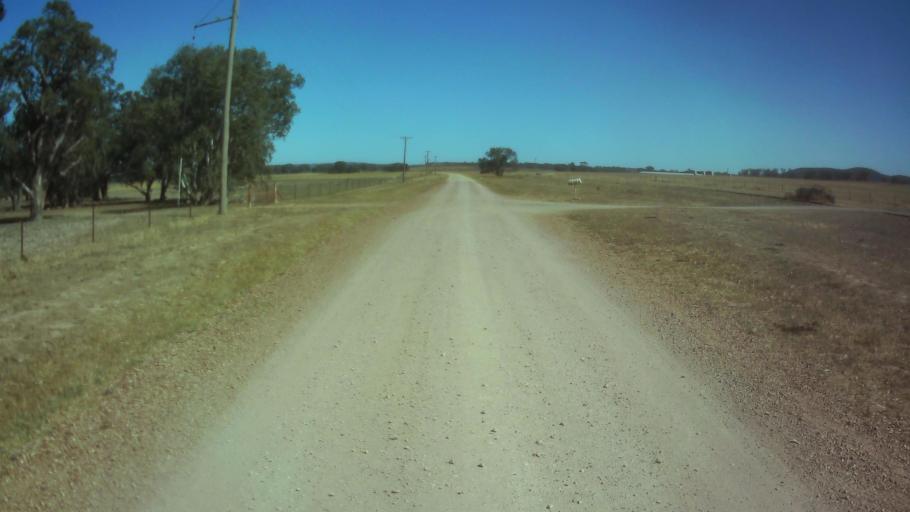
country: AU
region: New South Wales
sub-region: Weddin
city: Grenfell
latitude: -33.9411
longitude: 148.2896
